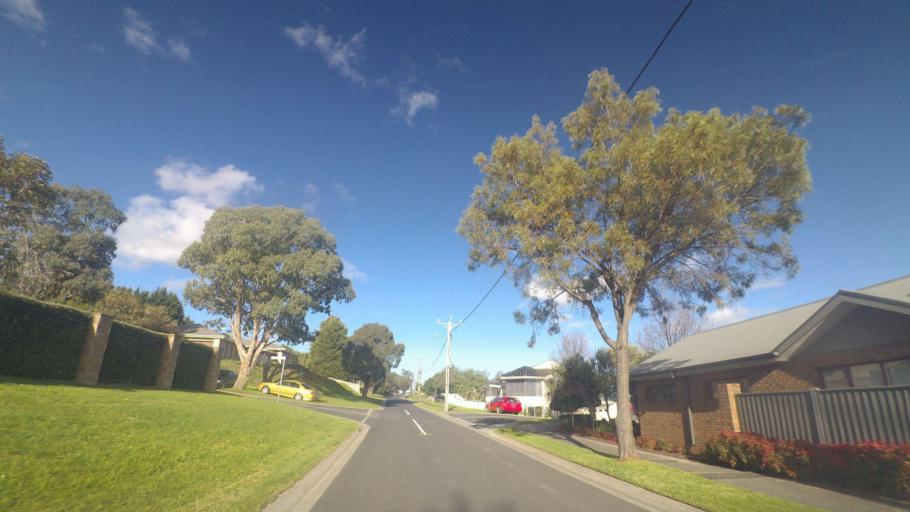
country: AU
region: Victoria
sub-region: Knox
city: Ferntree Gully
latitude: -37.9088
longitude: 145.2840
